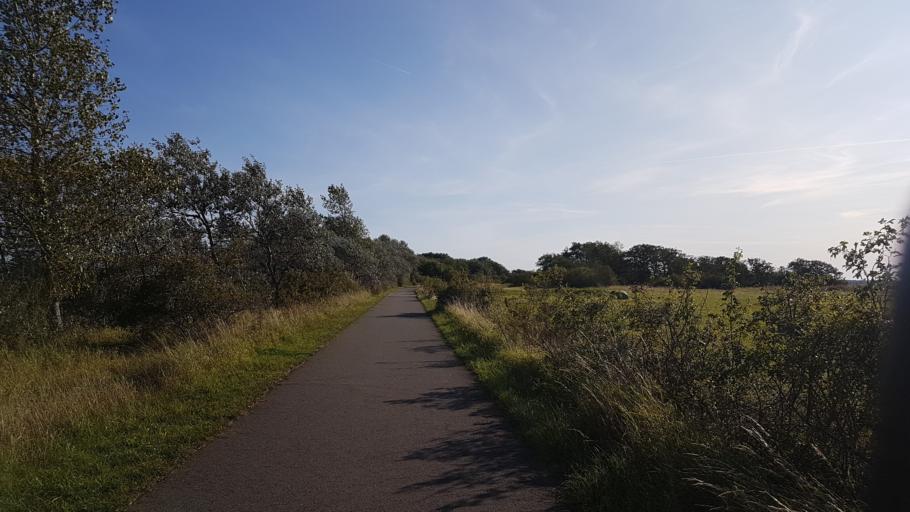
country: DE
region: Mecklenburg-Vorpommern
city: Wiek
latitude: 54.6382
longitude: 13.2913
